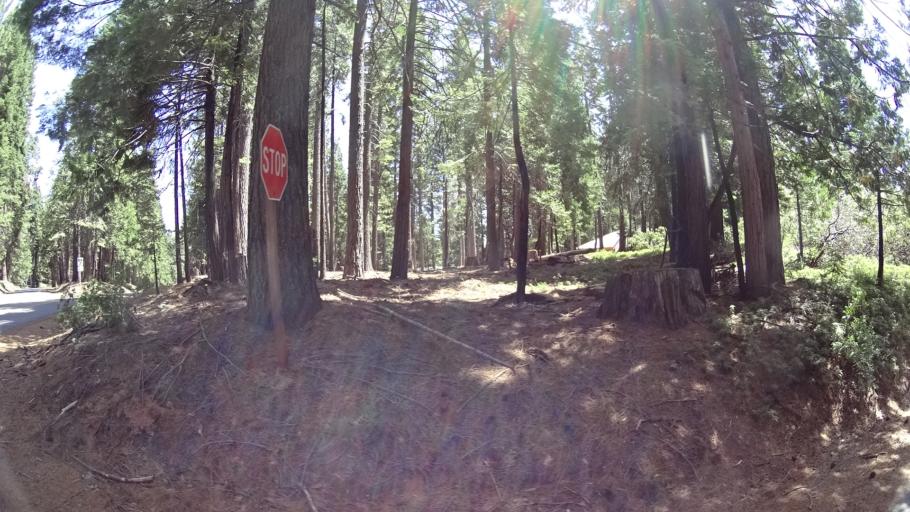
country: US
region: California
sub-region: Calaveras County
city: Arnold
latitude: 38.3053
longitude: -120.2674
